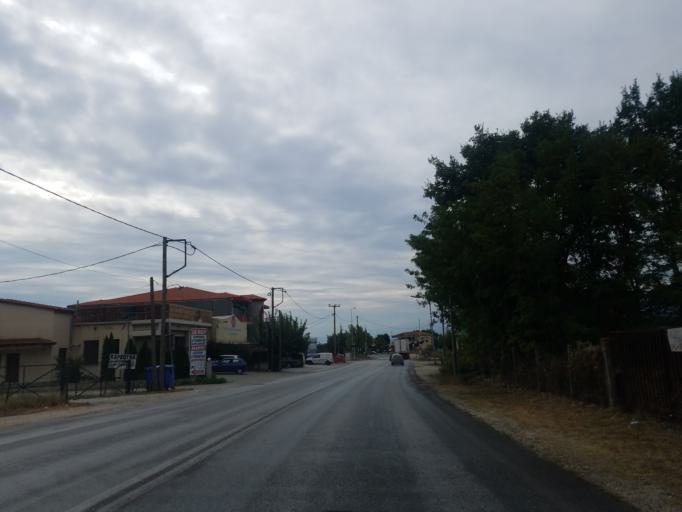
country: GR
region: Thessaly
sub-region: Trikala
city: Kalampaka
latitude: 39.6976
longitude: 21.6399
